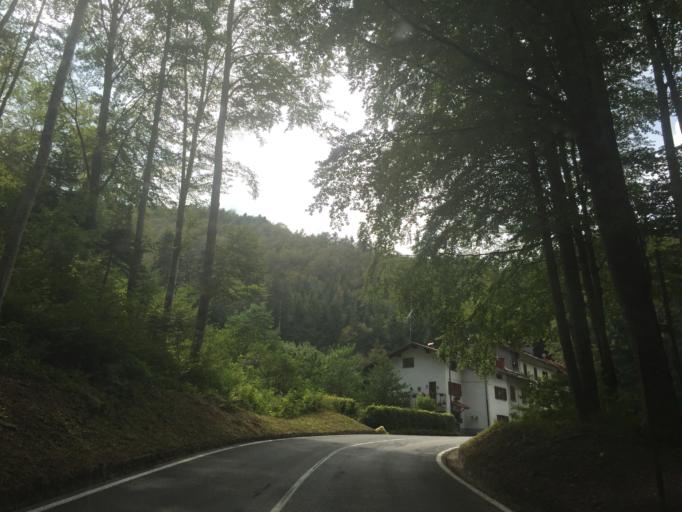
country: IT
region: Tuscany
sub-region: Provincia di Pistoia
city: Abetone
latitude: 44.1256
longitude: 10.6973
